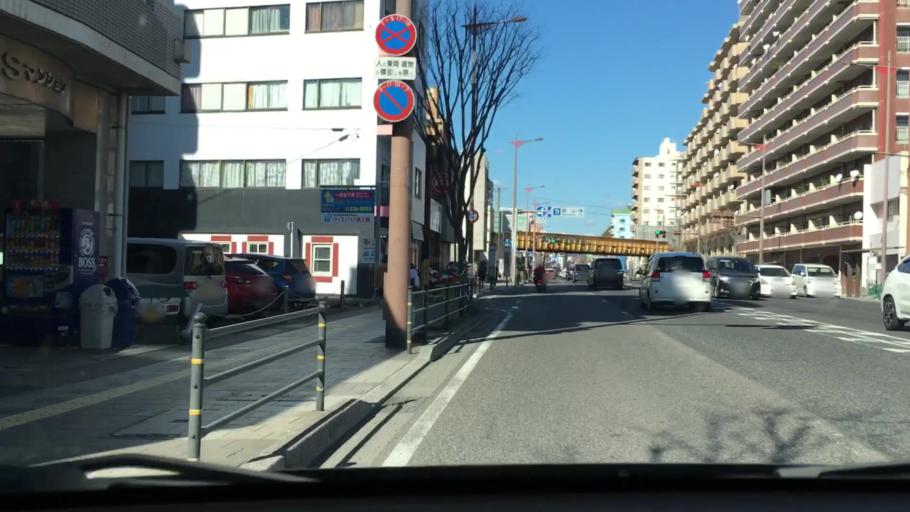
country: JP
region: Kagoshima
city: Kagoshima-shi
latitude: 31.5919
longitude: 130.5447
